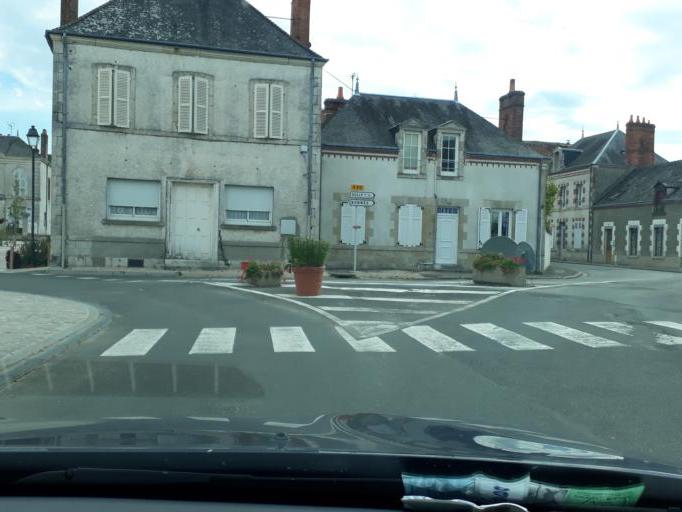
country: FR
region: Centre
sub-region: Departement du Loiret
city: Saint-Benoit-sur-Loire
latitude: 47.8098
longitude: 2.3073
